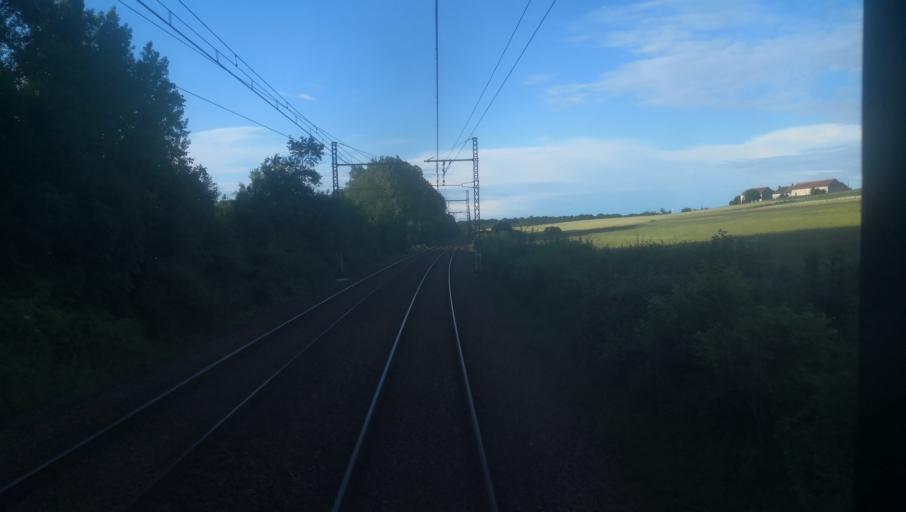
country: FR
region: Centre
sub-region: Departement de l'Indre
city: Reuilly
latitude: 47.0513
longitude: 2.0355
